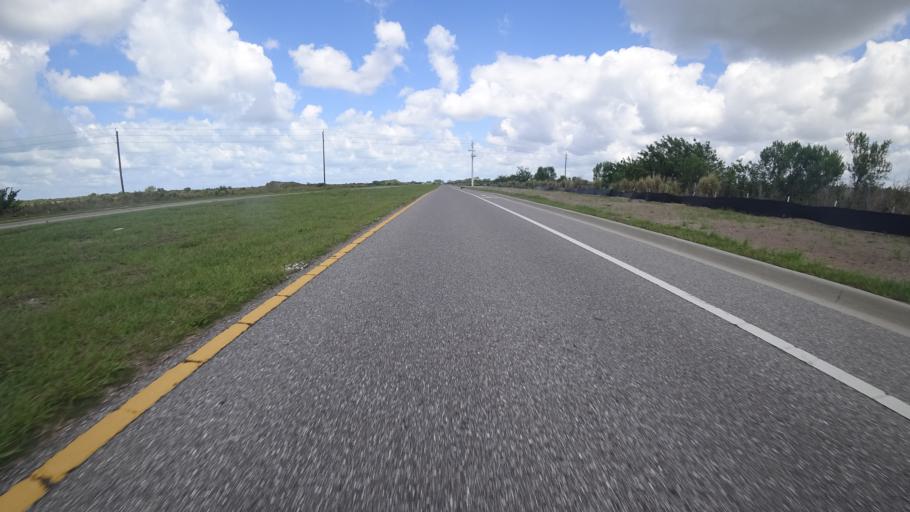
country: US
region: Florida
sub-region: Manatee County
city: Bayshore Gardens
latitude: 27.4370
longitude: -82.6237
